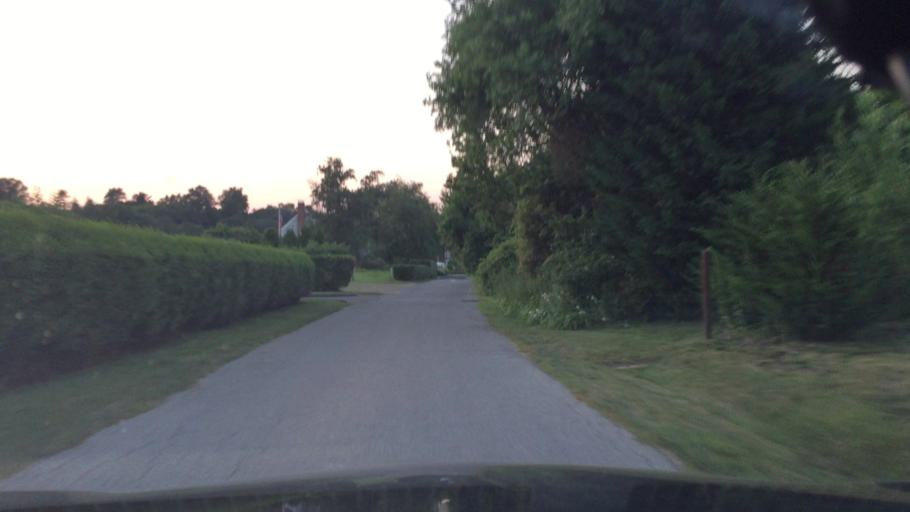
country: US
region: Connecticut
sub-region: Fairfield County
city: Darien
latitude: 41.0653
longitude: -73.4295
